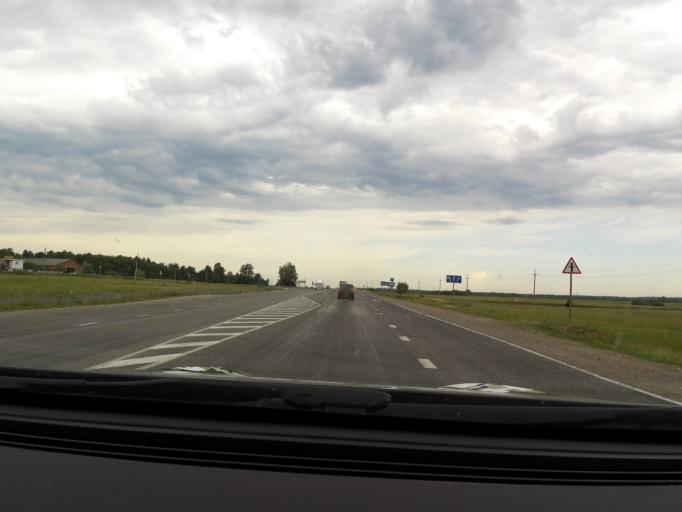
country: RU
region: Bashkortostan
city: Kudeyevskiy
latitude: 54.8170
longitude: 56.7604
